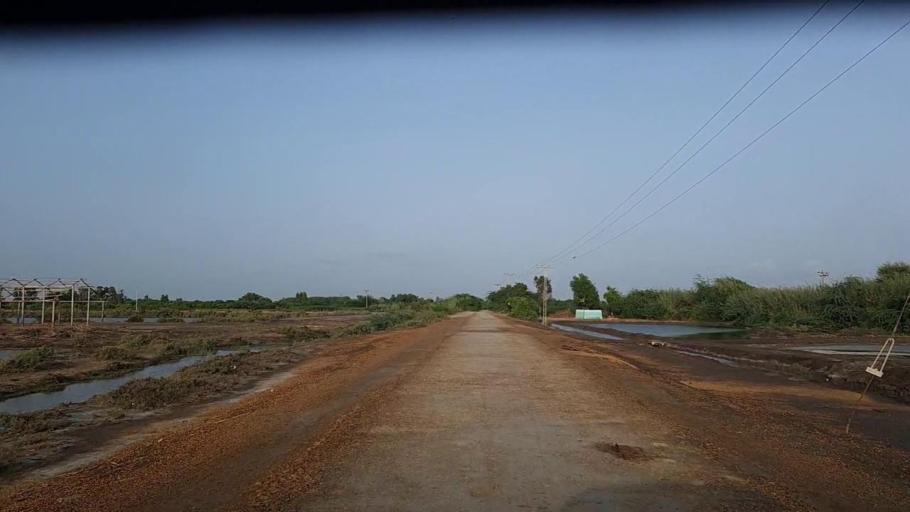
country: PK
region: Sindh
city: Thatta
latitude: 24.7599
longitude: 67.9129
